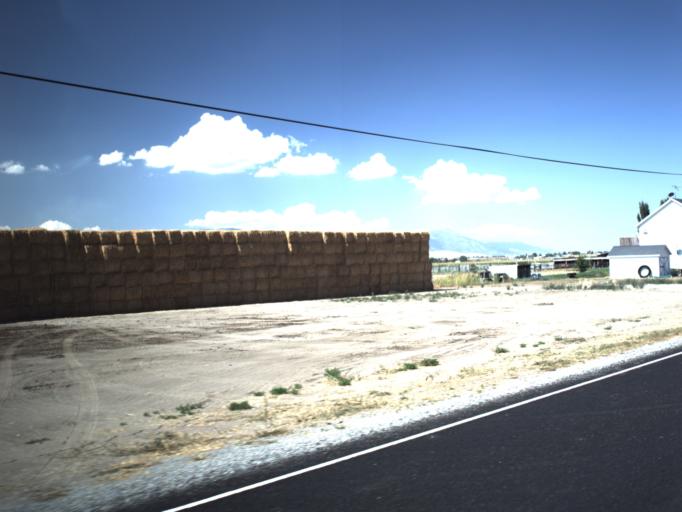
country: US
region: Utah
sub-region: Cache County
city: Lewiston
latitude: 41.9930
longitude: -111.8765
